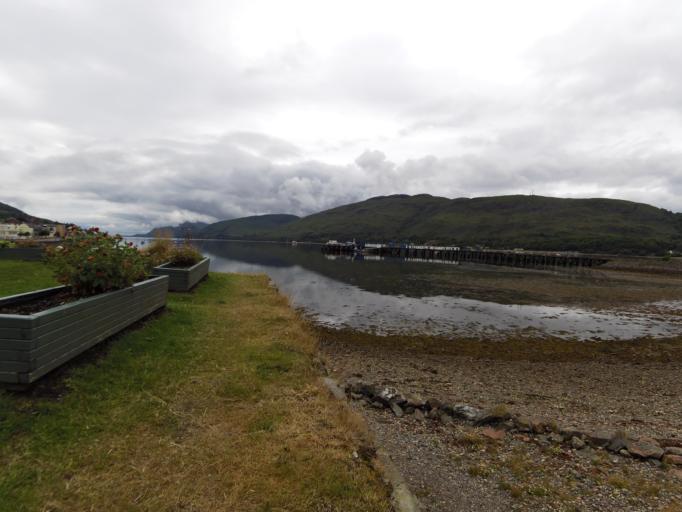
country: GB
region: Scotland
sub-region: Highland
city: Fort William
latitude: 56.8214
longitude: -5.1082
